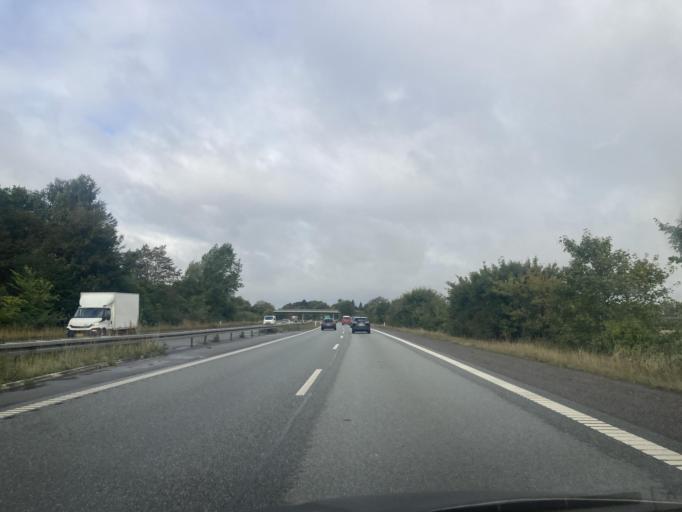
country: DK
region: Zealand
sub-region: Lejre Kommune
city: Lejre
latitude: 55.6380
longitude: 11.9552
